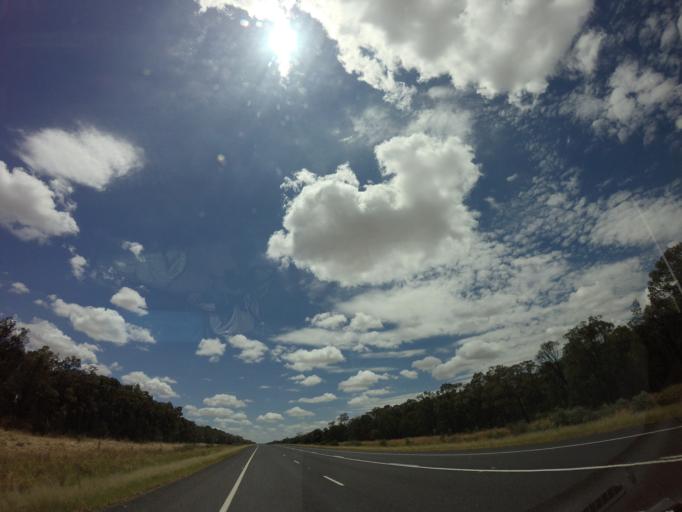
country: AU
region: New South Wales
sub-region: Moree Plains
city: Boggabilla
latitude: -28.8665
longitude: 150.1933
